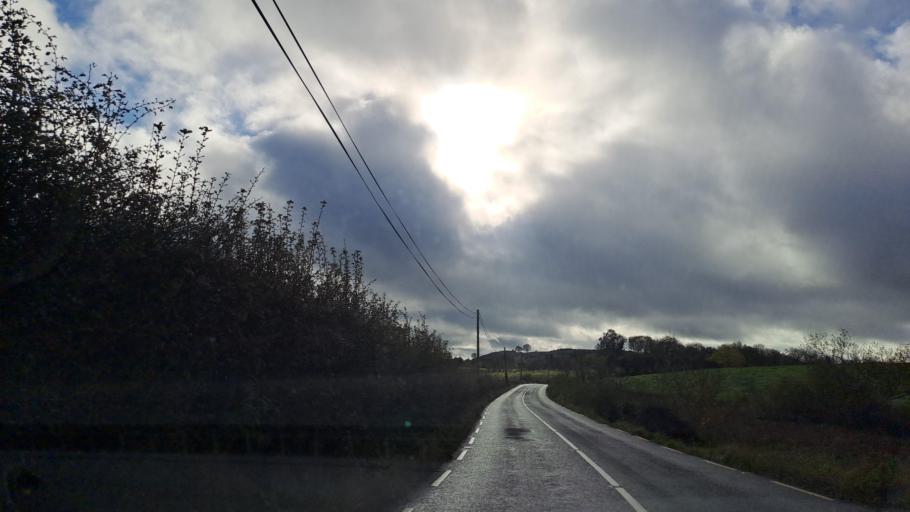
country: IE
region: Ulster
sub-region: An Cabhan
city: Virginia
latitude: 53.8709
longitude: -7.0407
